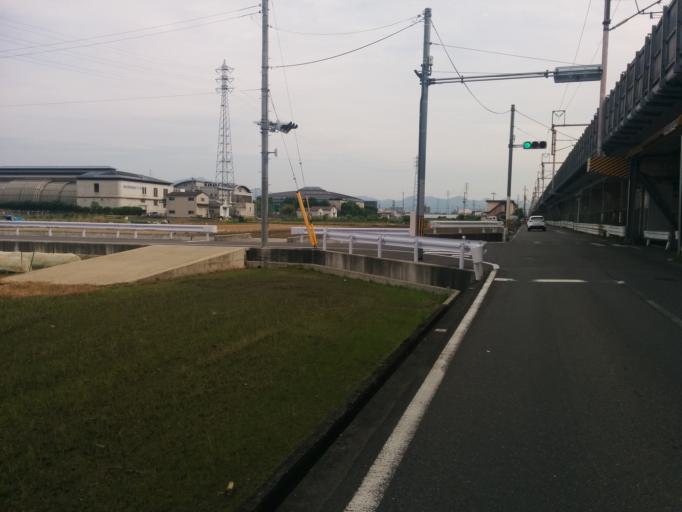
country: JP
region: Kyoto
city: Muko
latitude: 34.9425
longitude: 135.7144
